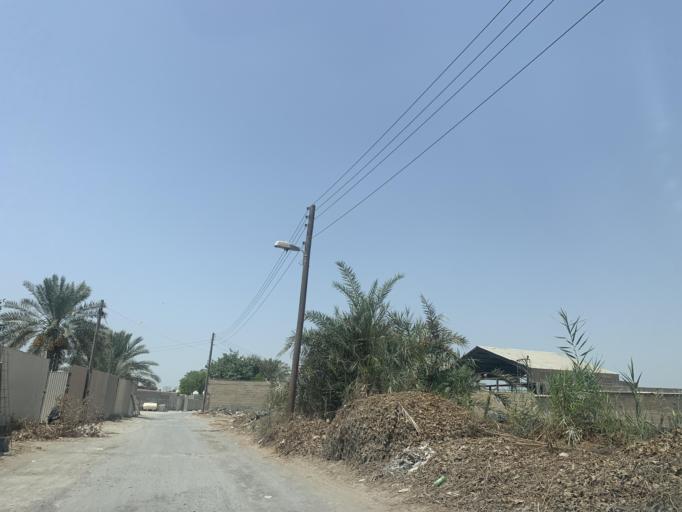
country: BH
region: Central Governorate
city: Madinat Hamad
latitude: 26.1547
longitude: 50.4966
